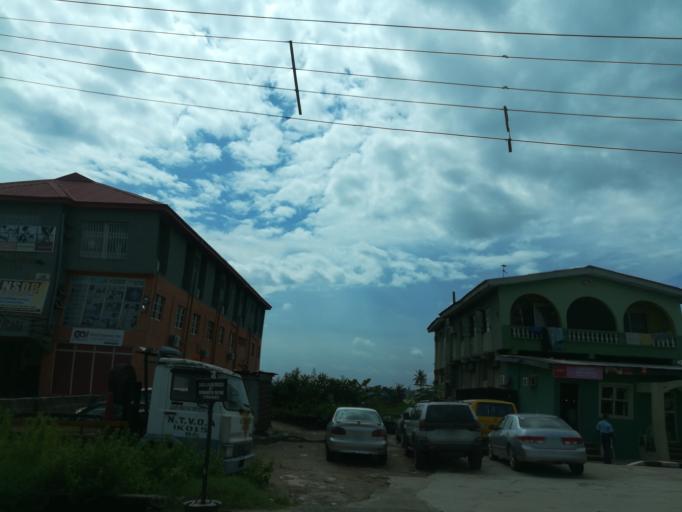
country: NG
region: Lagos
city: Ikorodu
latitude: 6.6132
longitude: 3.5013
